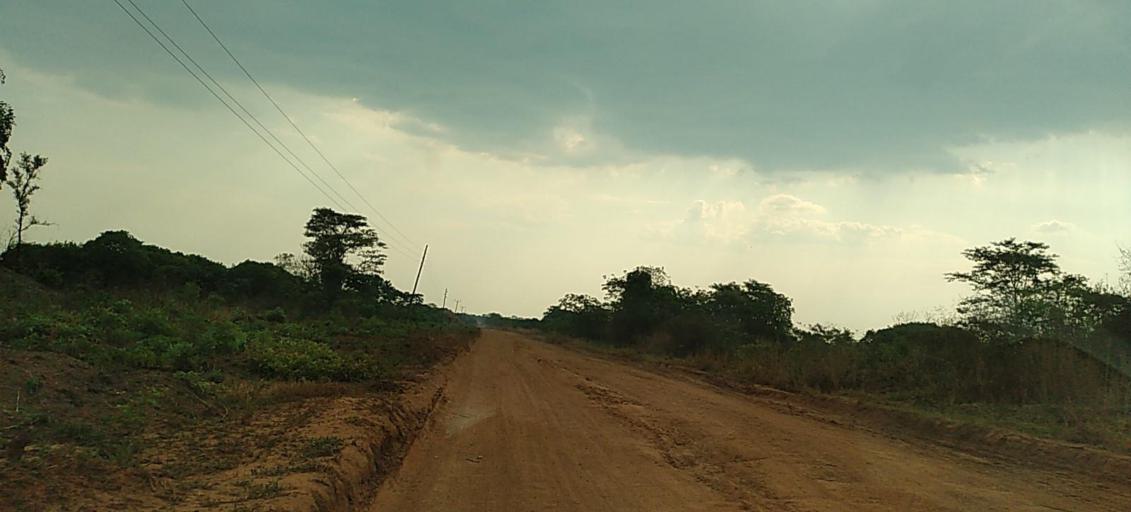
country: ZM
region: Copperbelt
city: Kalulushi
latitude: -12.9461
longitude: 27.9160
